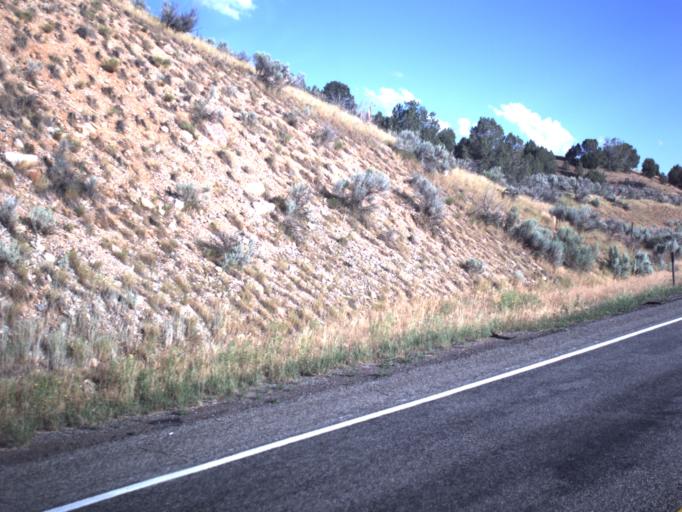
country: US
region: Utah
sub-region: Utah County
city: Woodland Hills
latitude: 39.9142
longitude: -111.5507
